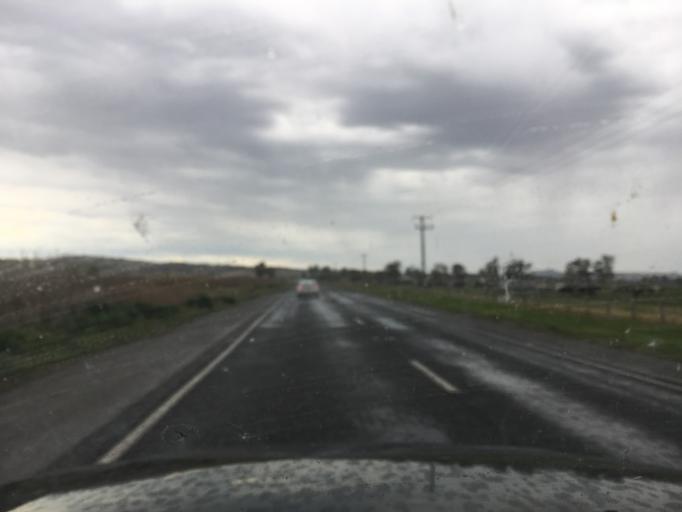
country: AU
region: New South Wales
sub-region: Muswellbrook
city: Muswellbrook
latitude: -32.2232
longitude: 150.9007
